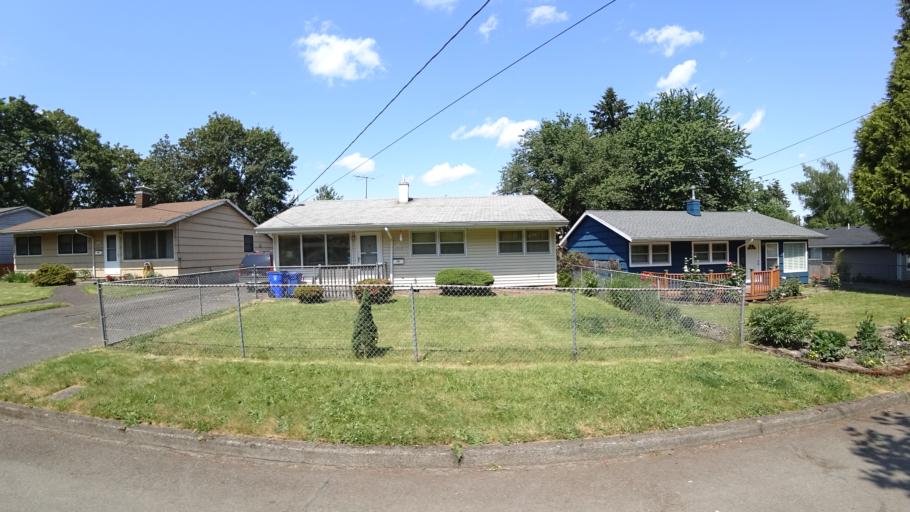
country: US
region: Oregon
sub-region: Washington County
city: West Haven
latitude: 45.5966
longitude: -122.7404
